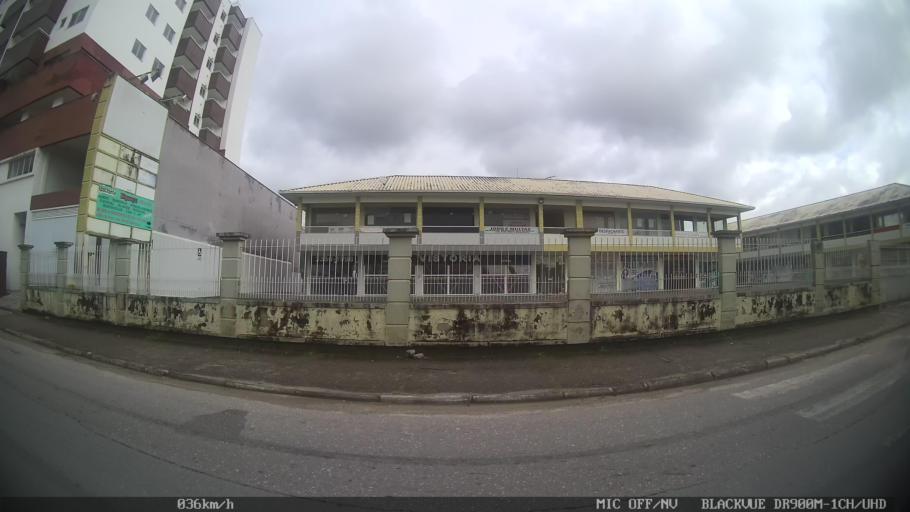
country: BR
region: Santa Catarina
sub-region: Biguacu
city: Biguacu
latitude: -27.5055
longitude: -48.6526
